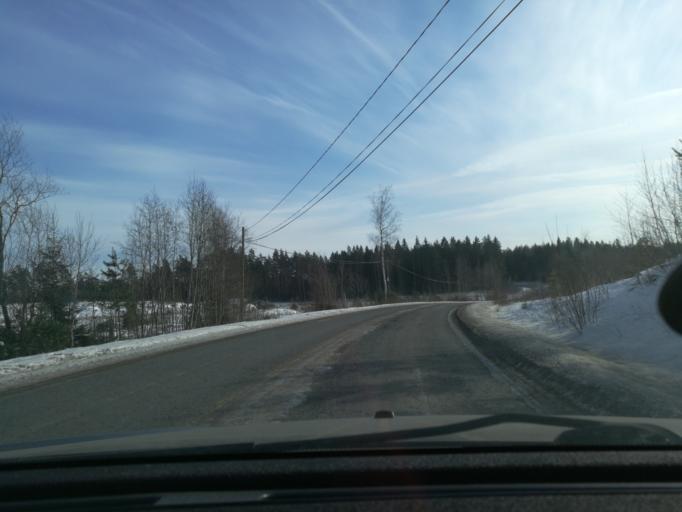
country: FI
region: Uusimaa
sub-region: Helsinki
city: Saukkola
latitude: 60.4514
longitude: 24.0050
